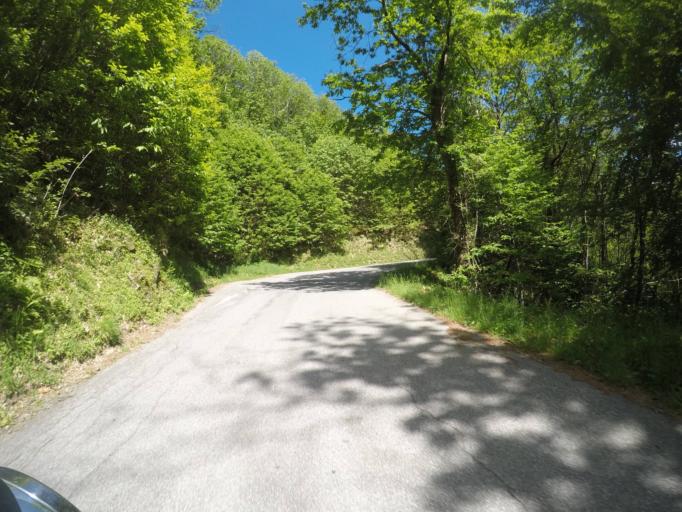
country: IT
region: Tuscany
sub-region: Provincia di Lucca
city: Careggine
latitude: 44.0938
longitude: 10.3246
